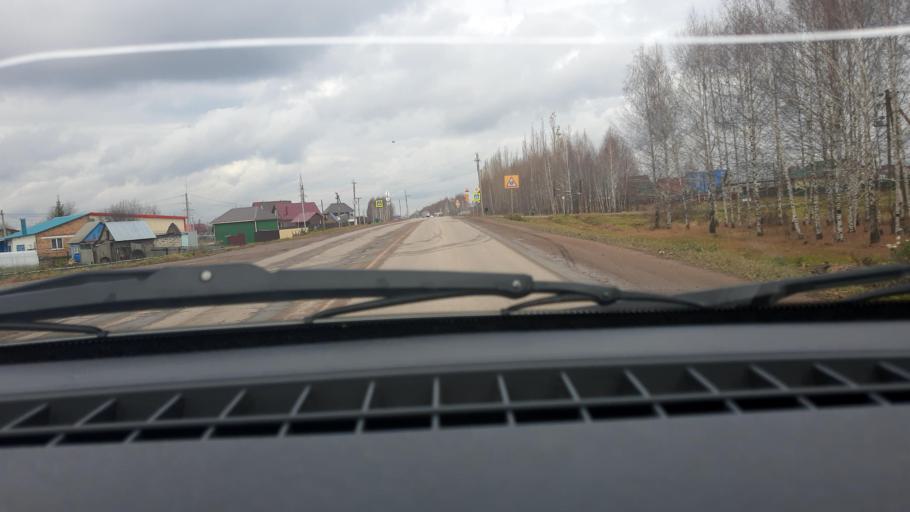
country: RU
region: Bashkortostan
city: Iglino
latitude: 54.8179
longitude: 56.4186
